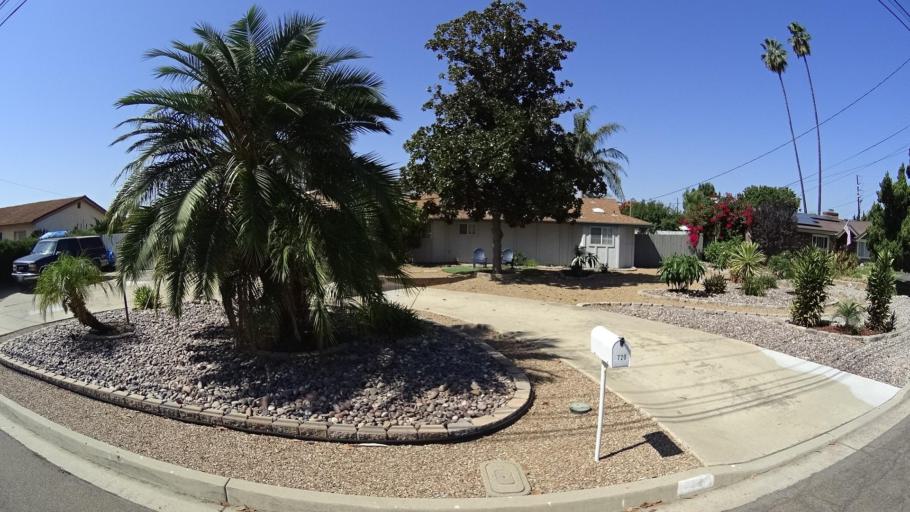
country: US
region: California
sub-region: San Diego County
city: Granite Hills
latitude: 32.8030
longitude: -116.9199
